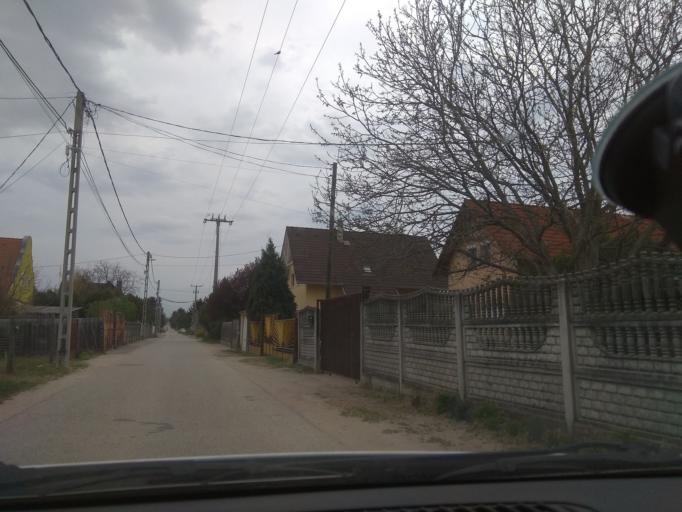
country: HU
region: Pest
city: Halasztelek
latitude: 47.3742
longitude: 19.0169
